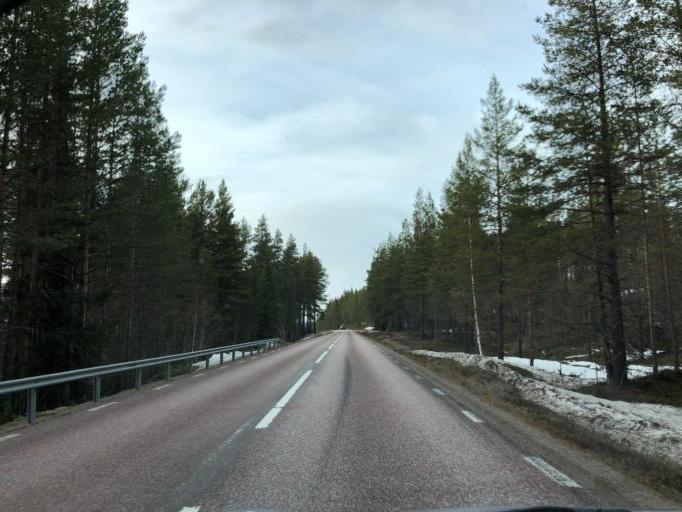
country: NO
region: Hedmark
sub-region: Trysil
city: Innbygda
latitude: 61.7723
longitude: 12.9503
